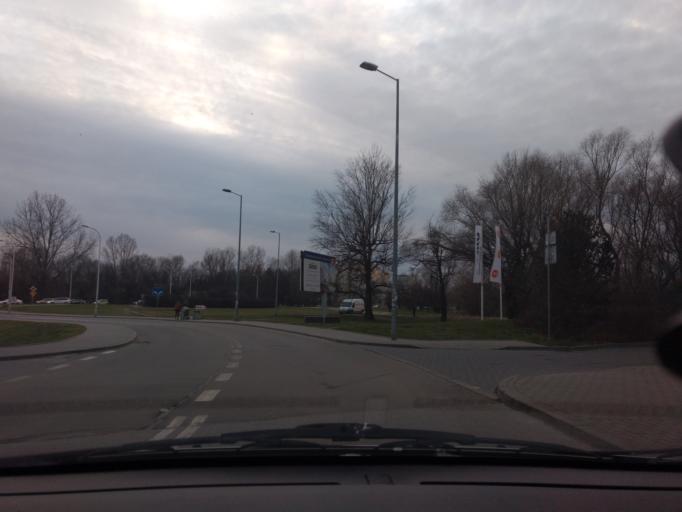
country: PL
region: Masovian Voivodeship
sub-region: Warszawa
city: Praga Poludnie
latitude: 52.2273
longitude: 21.0777
